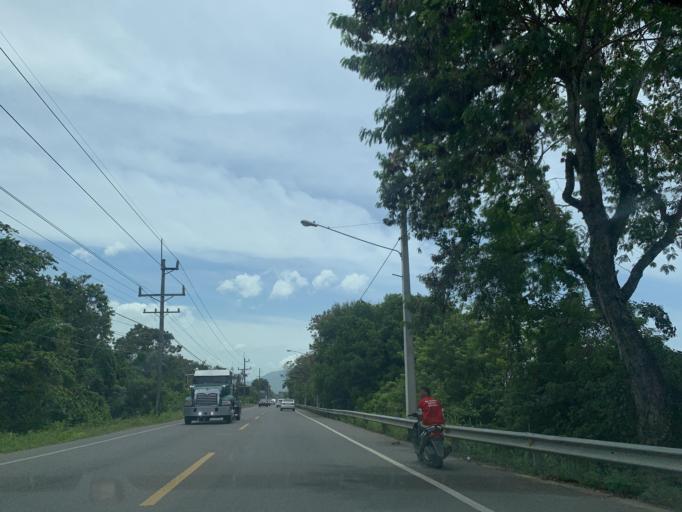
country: DO
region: Puerto Plata
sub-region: Puerto Plata
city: Puerto Plata
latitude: 19.7500
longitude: -70.5668
